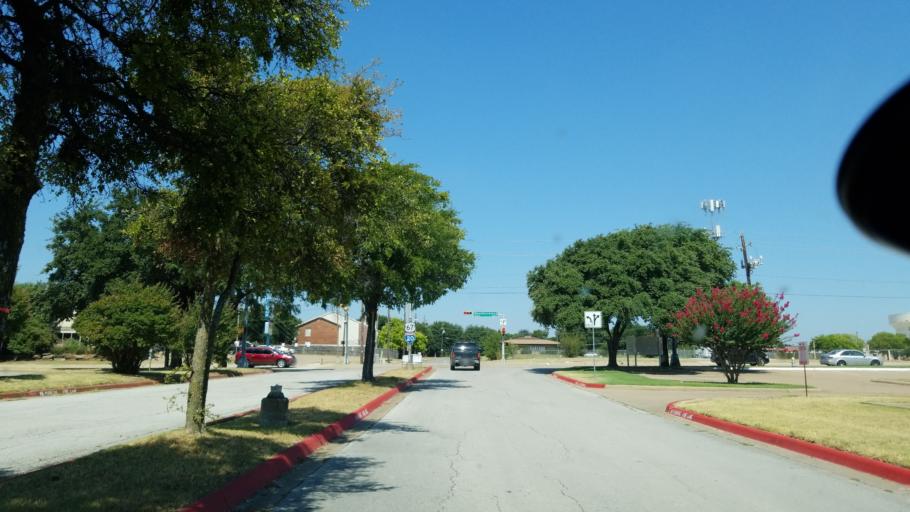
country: US
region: Texas
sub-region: Dallas County
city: Duncanville
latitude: 32.6589
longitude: -96.8824
